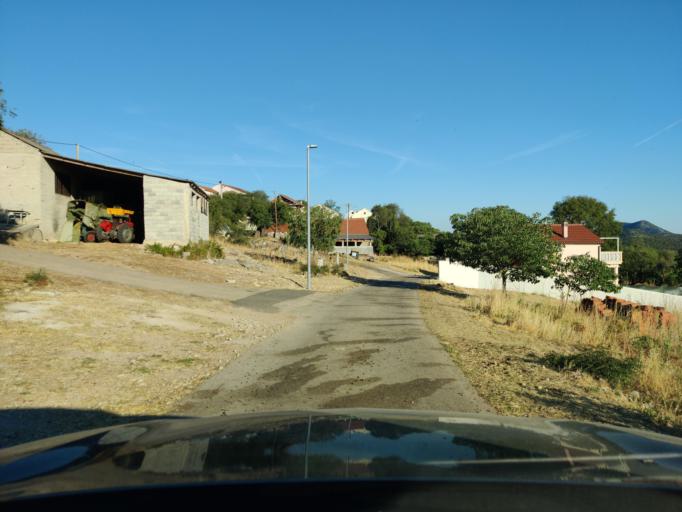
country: HR
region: Sibensko-Kniniska
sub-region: Grad Sibenik
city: Pirovac
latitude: 43.8639
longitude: 15.7165
